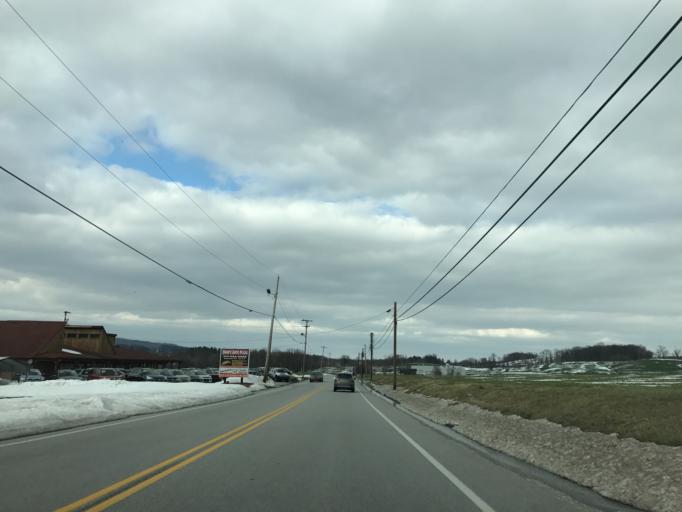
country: US
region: Pennsylvania
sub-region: York County
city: Parkville
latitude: 39.8215
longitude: -76.9378
